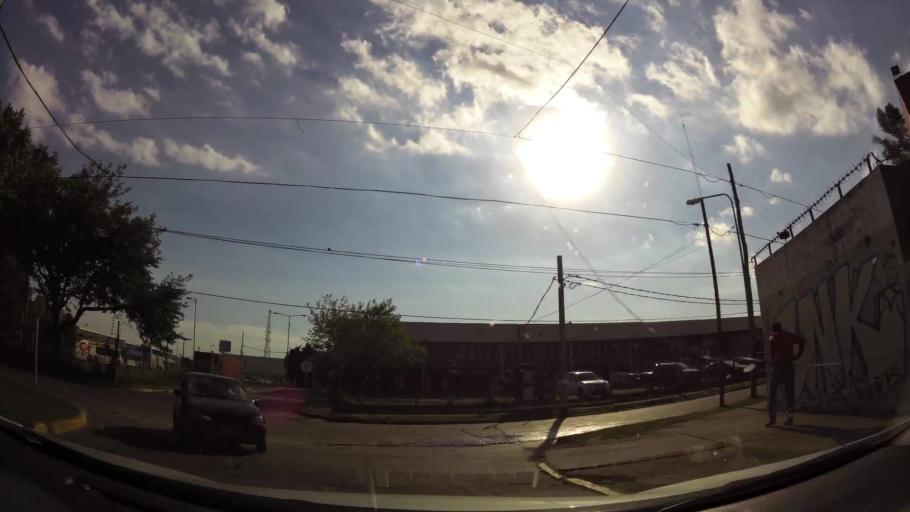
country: AR
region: Buenos Aires
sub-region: Partido de Tigre
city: Tigre
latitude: -34.4730
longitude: -58.6550
